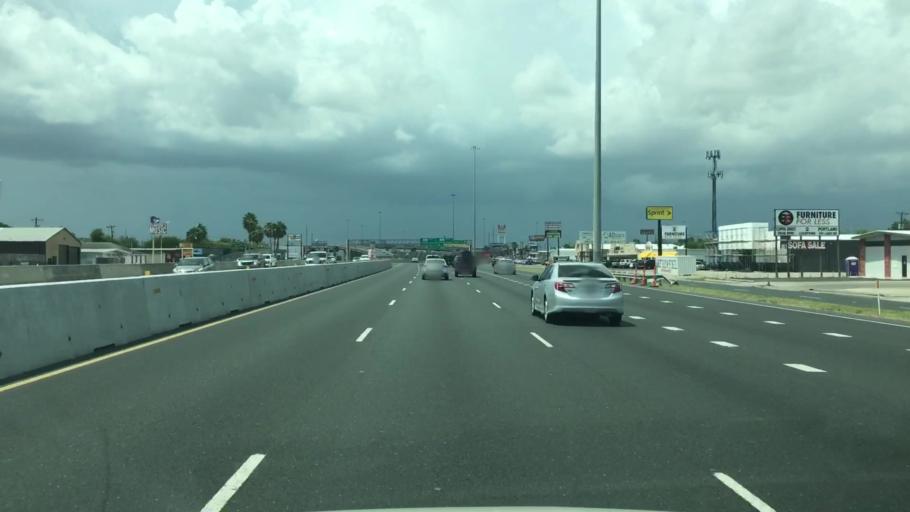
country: US
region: Texas
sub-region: Nueces County
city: Corpus Christi
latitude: 27.7322
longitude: -97.4204
